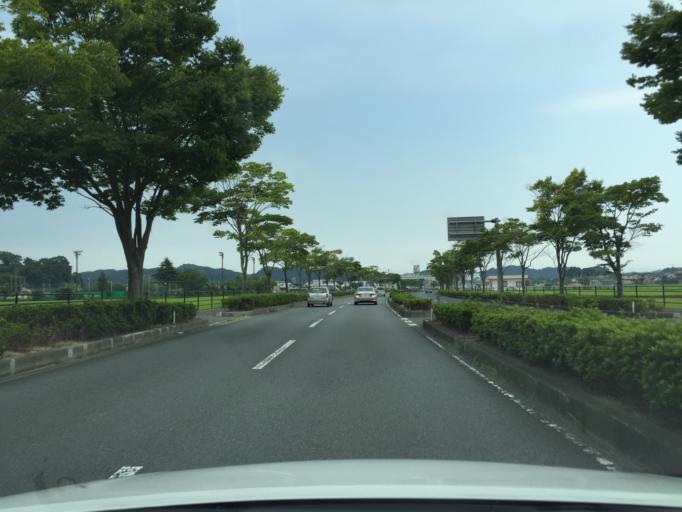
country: JP
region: Fukushima
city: Iwaki
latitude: 36.9852
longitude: 140.8487
